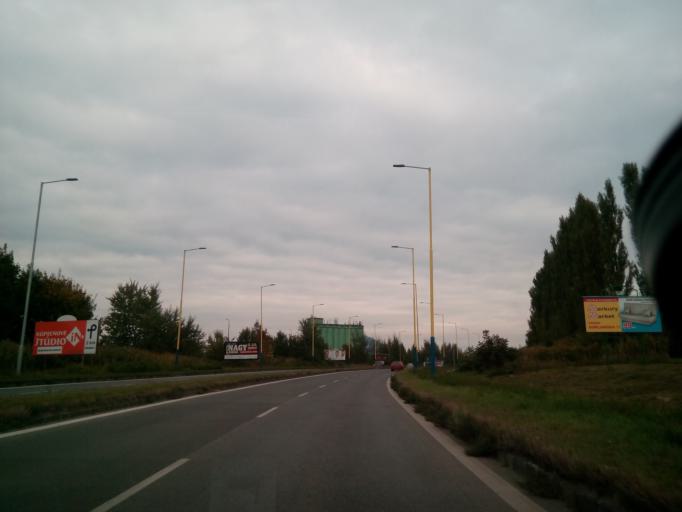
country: SK
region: Presovsky
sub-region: Okres Presov
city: Presov
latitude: 49.0065
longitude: 21.2653
